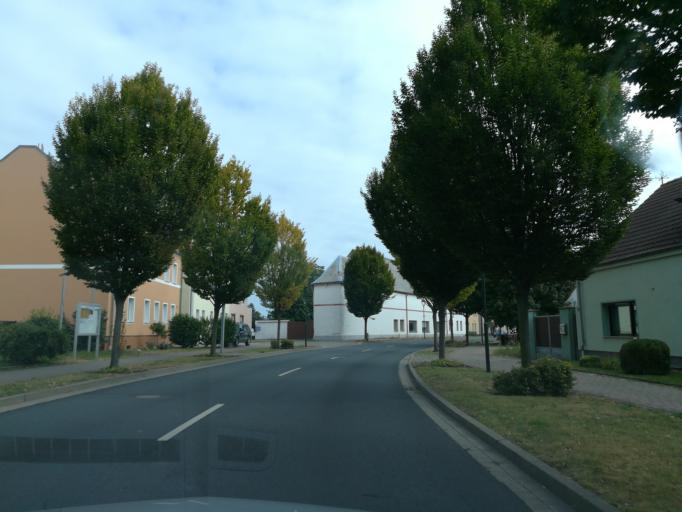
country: DE
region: Saxony-Anhalt
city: Ebendorf
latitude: 52.1822
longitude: 11.5748
